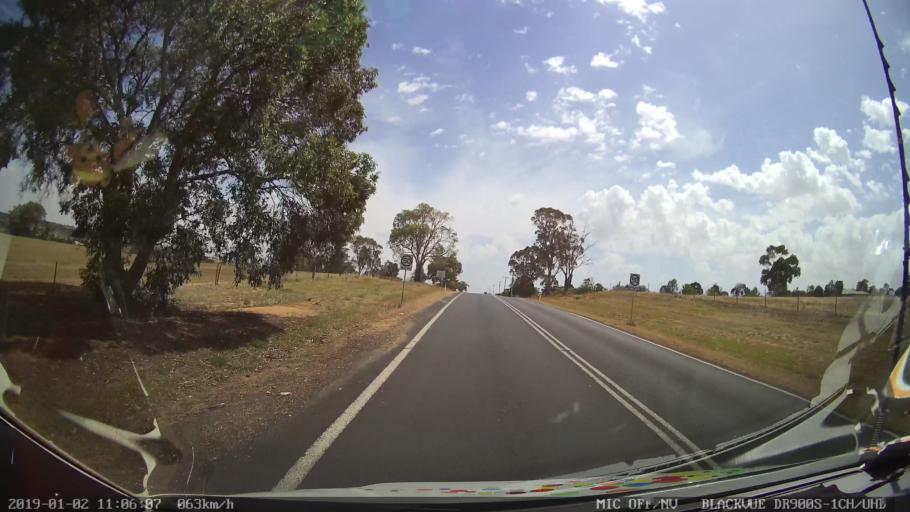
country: AU
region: New South Wales
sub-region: Young
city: Young
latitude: -34.5576
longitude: 148.3555
